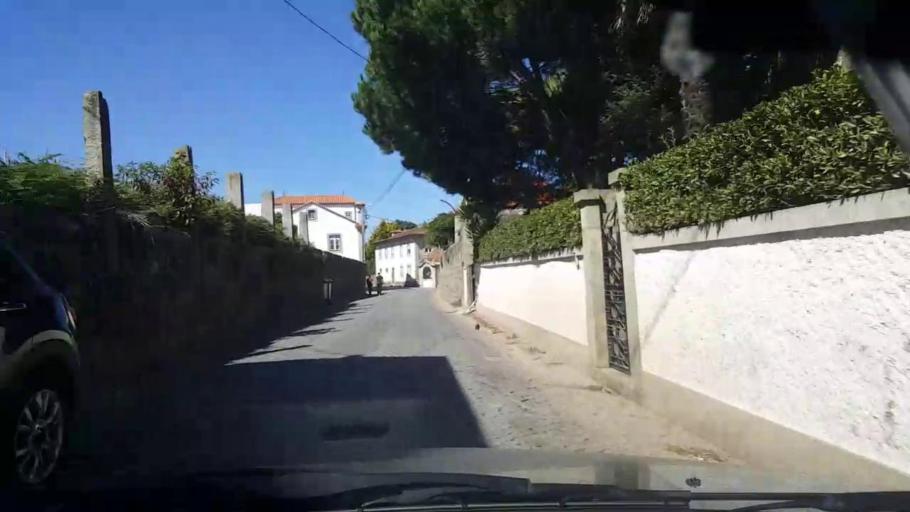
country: PT
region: Porto
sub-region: Vila do Conde
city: Arvore
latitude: 41.3231
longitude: -8.7027
